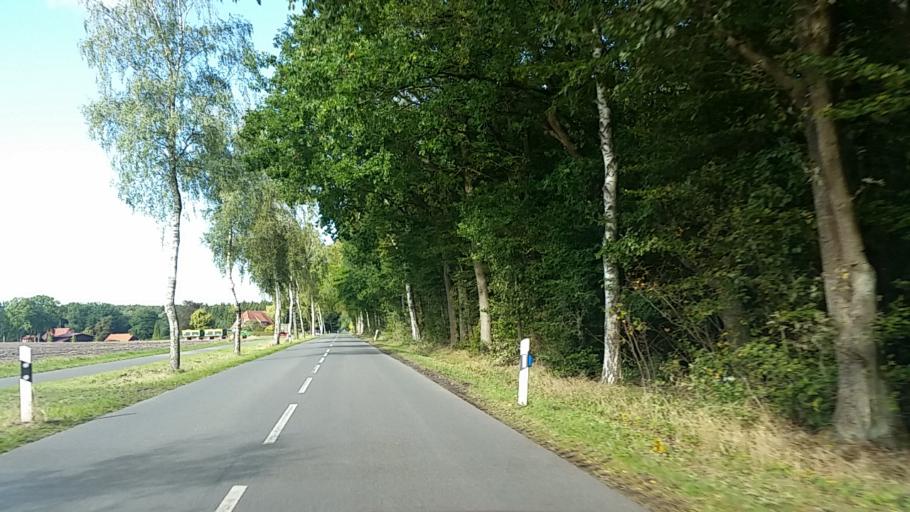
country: DE
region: Lower Saxony
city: Neuenkirchen
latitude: 53.0310
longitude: 9.7352
